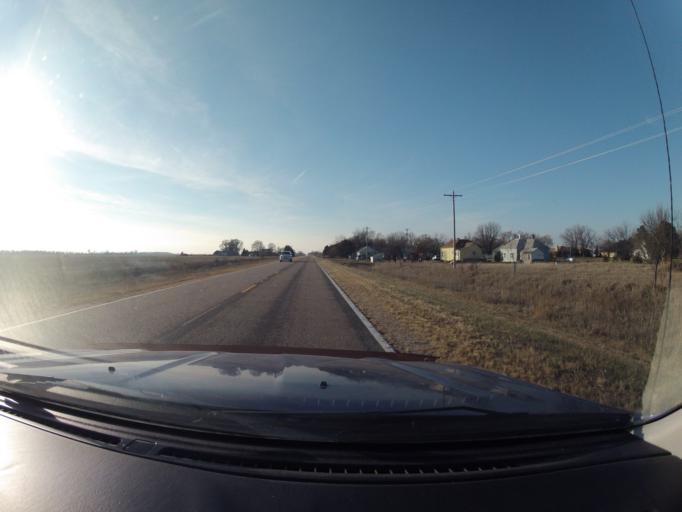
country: US
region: Nebraska
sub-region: Buffalo County
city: Kearney
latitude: 40.6410
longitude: -98.9619
